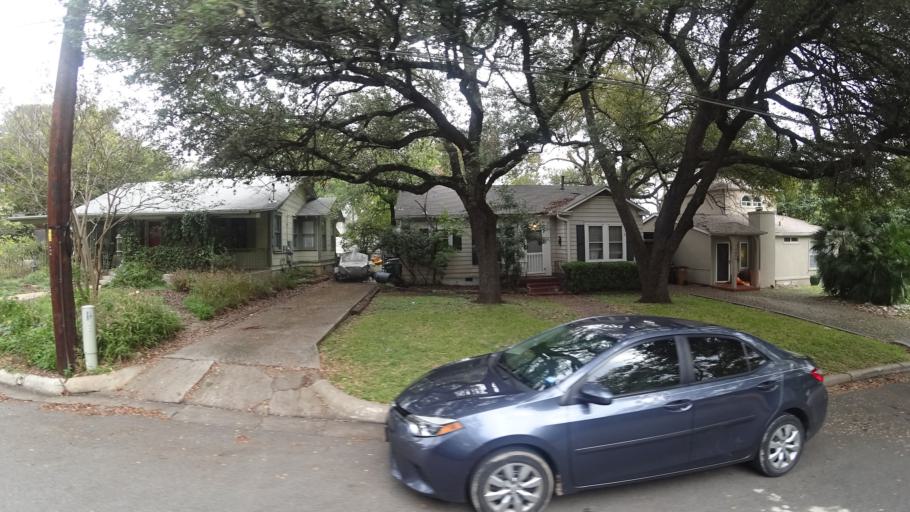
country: US
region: Texas
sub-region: Travis County
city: Austin
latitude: 30.2585
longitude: -97.7618
